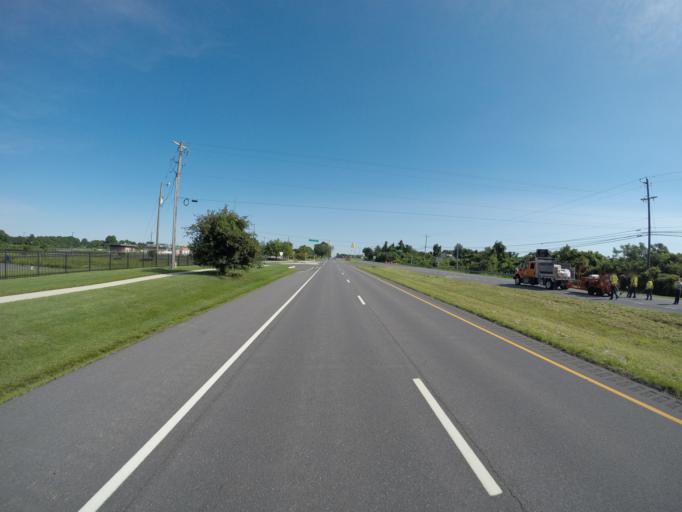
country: US
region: Delaware
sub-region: New Castle County
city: Bear
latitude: 39.5746
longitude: -75.6564
